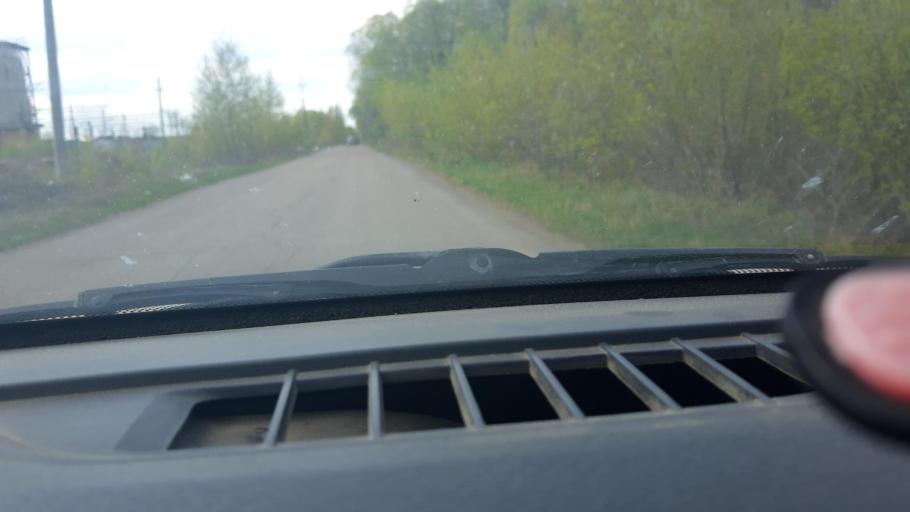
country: RU
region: Bashkortostan
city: Avdon
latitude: 54.6556
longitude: 55.8262
